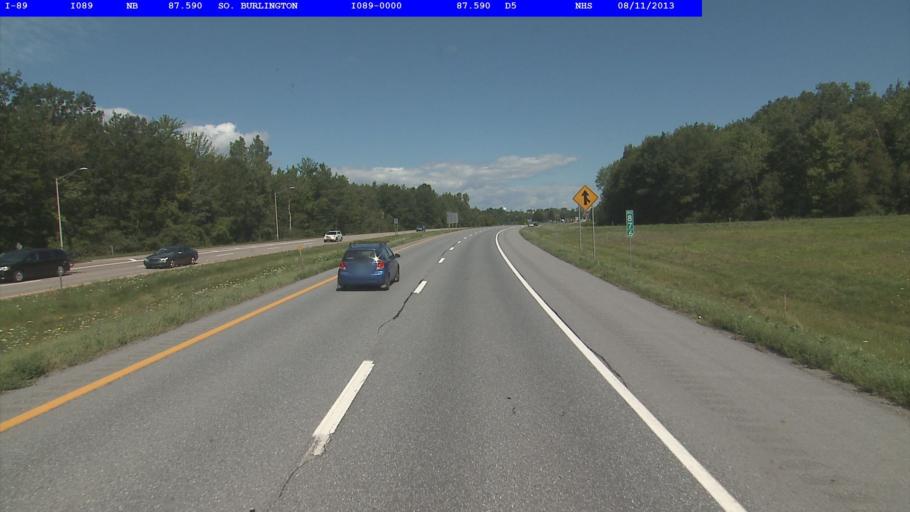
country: US
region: Vermont
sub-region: Chittenden County
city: South Burlington
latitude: 44.4538
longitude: -73.1833
